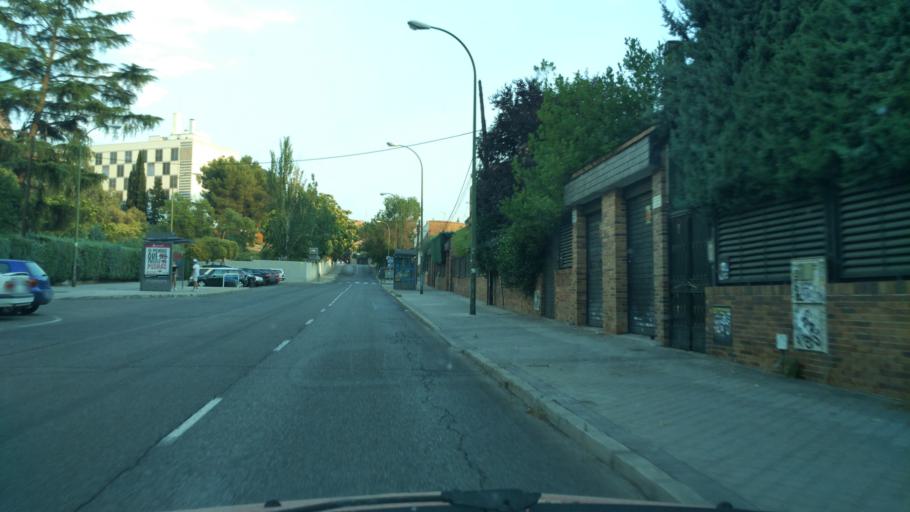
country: ES
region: Madrid
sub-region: Provincia de Madrid
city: Tetuan de las Victorias
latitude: 40.4702
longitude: -3.7265
